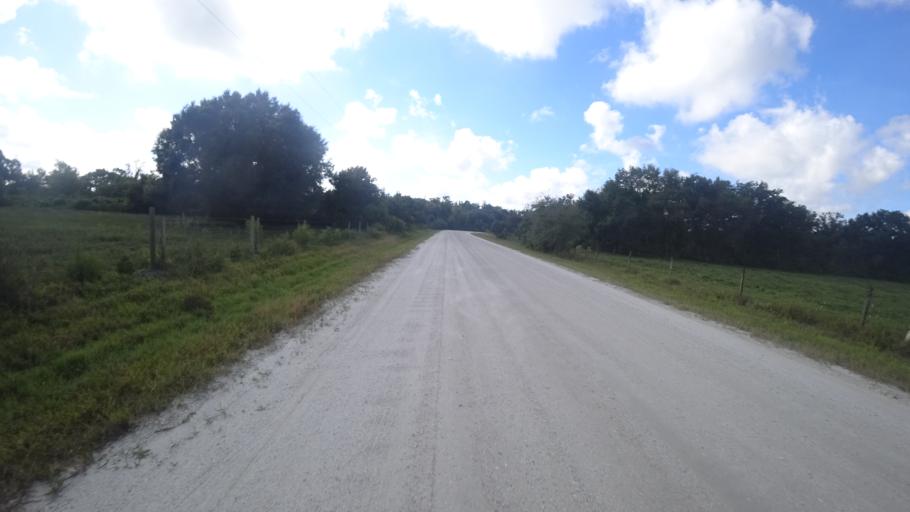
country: US
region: Florida
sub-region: Sarasota County
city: Lake Sarasota
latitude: 27.3286
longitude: -82.2041
